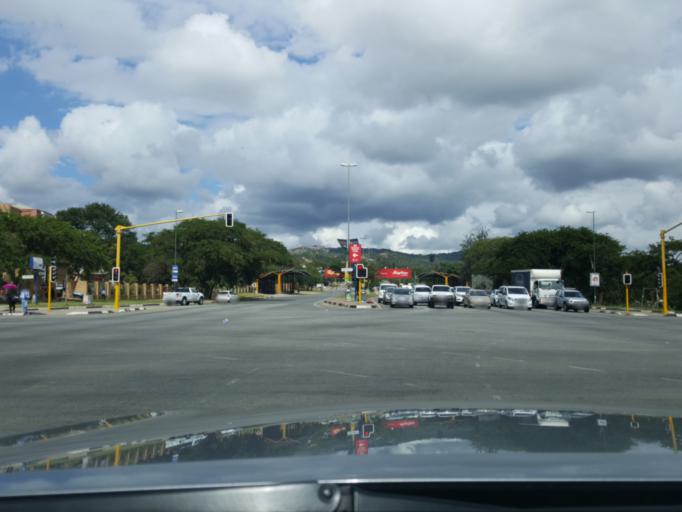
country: ZA
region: Mpumalanga
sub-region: Ehlanzeni District
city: Nelspruit
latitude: -25.4749
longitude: 30.9695
